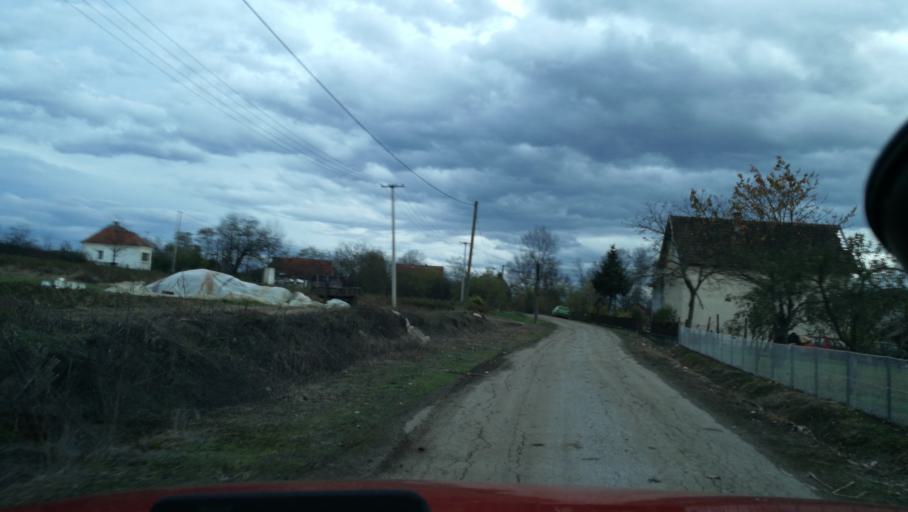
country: RS
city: Prislonica
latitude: 43.9066
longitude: 20.4306
